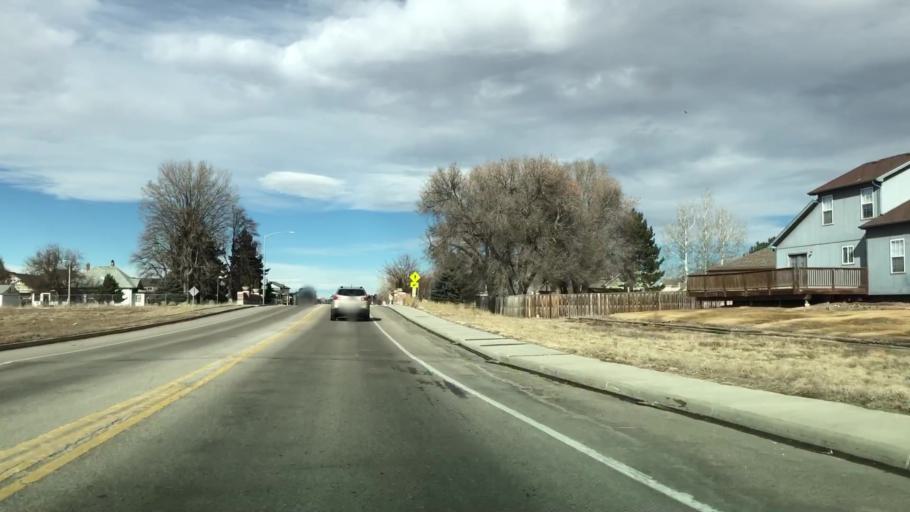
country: US
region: Colorado
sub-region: Weld County
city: Windsor
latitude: 40.4830
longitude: -104.9264
